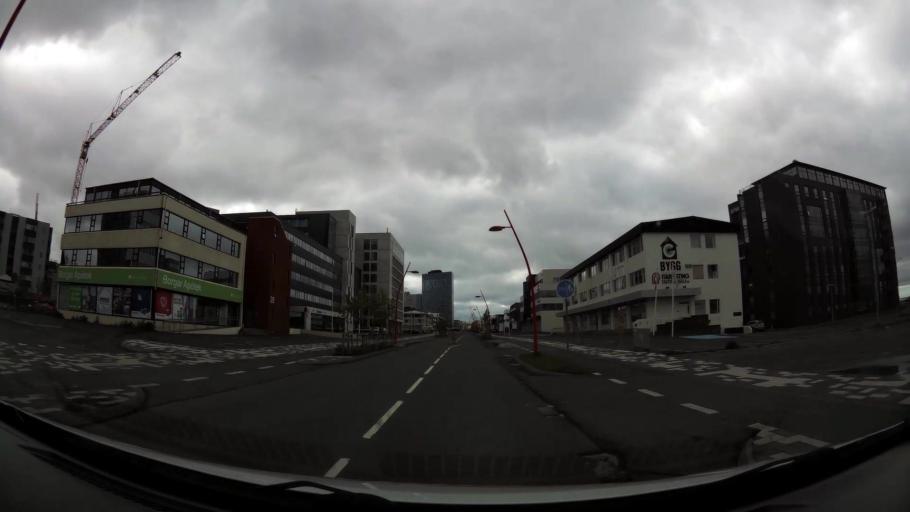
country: IS
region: Capital Region
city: Reykjavik
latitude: 64.1461
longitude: -21.8965
